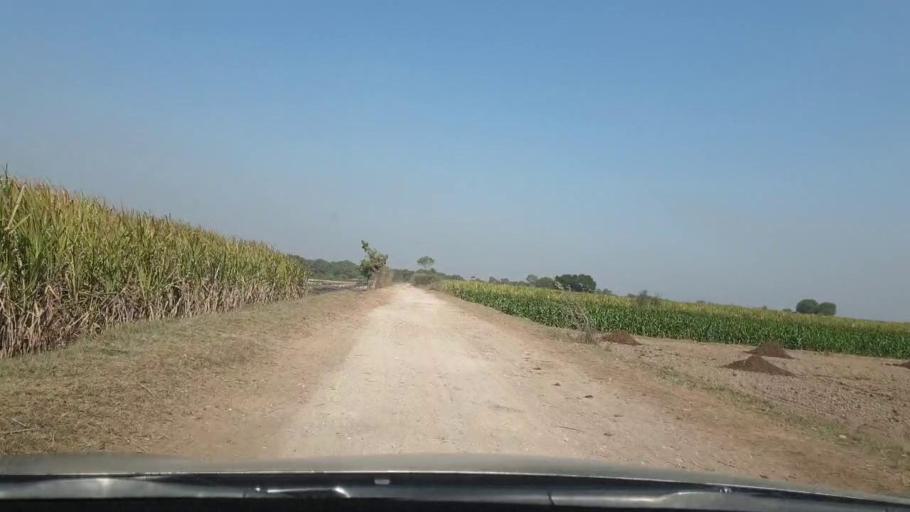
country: PK
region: Sindh
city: Tando Allahyar
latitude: 25.5947
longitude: 68.6407
